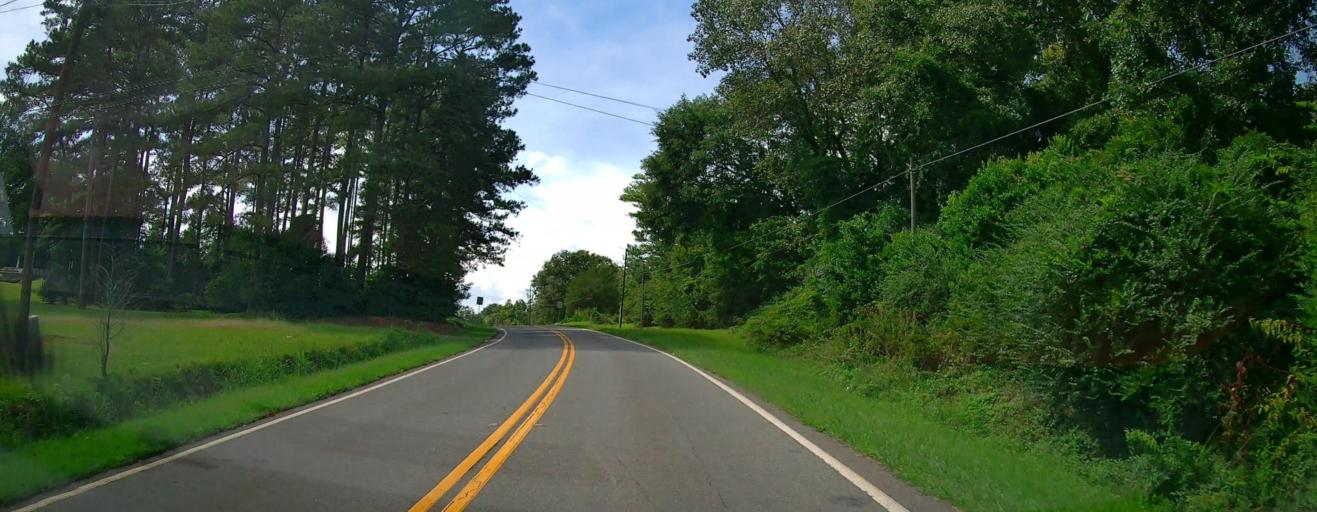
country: US
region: Georgia
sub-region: Talbot County
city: Talbotton
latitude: 32.6743
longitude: -84.5329
